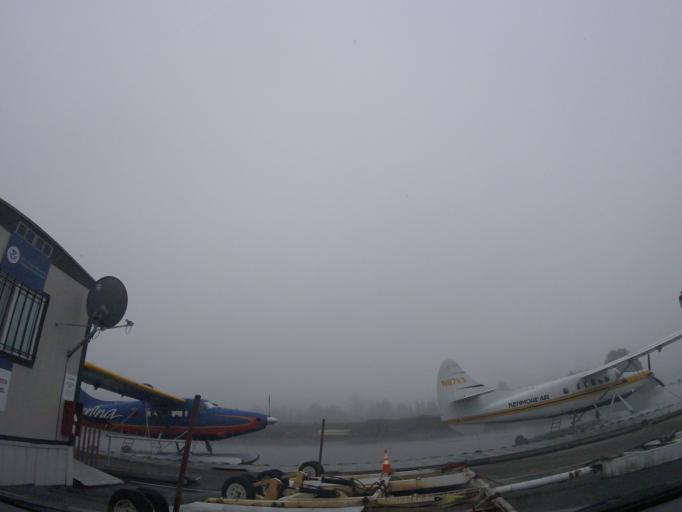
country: US
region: Washington
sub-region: King County
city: Kenmore
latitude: 47.7569
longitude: -122.2575
